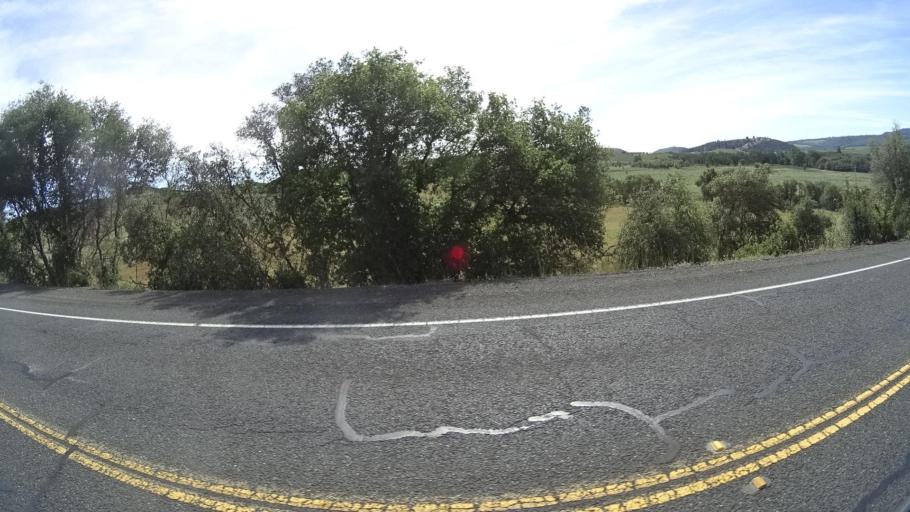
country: US
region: California
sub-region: Lake County
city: Soda Bay
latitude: 38.9343
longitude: -122.7404
